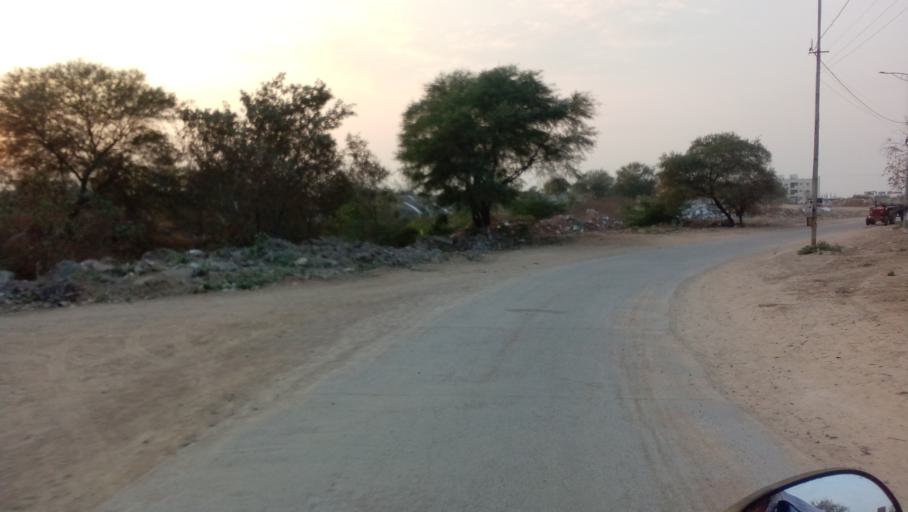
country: IN
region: Telangana
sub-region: Medak
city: Serilingampalle
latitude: 17.5192
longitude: 78.3050
